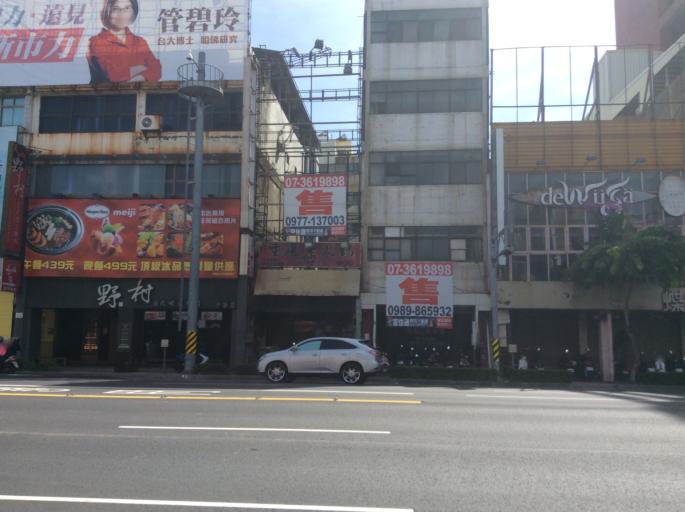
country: TW
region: Kaohsiung
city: Kaohsiung
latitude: 22.6332
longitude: 120.2944
